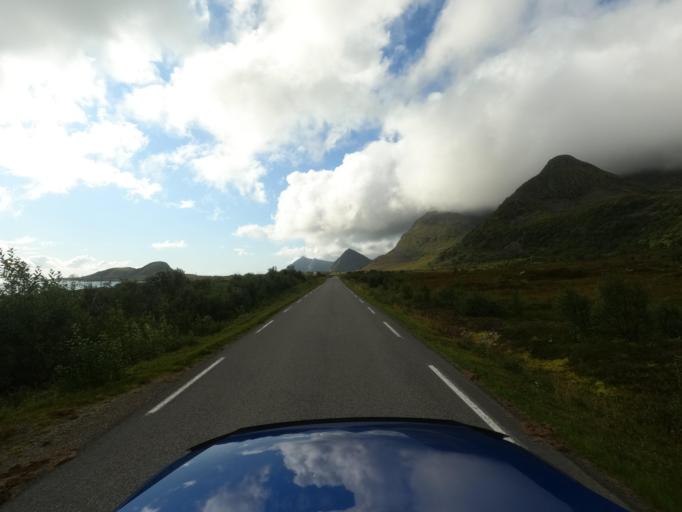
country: NO
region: Nordland
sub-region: Vagan
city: Kabelvag
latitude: 68.2461
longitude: 14.1321
